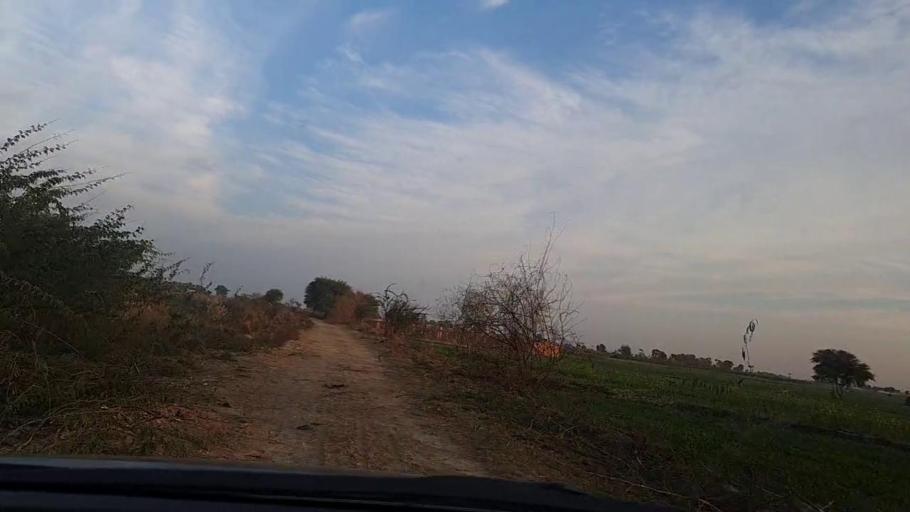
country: PK
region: Sindh
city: Sakrand
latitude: 26.1712
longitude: 68.3484
